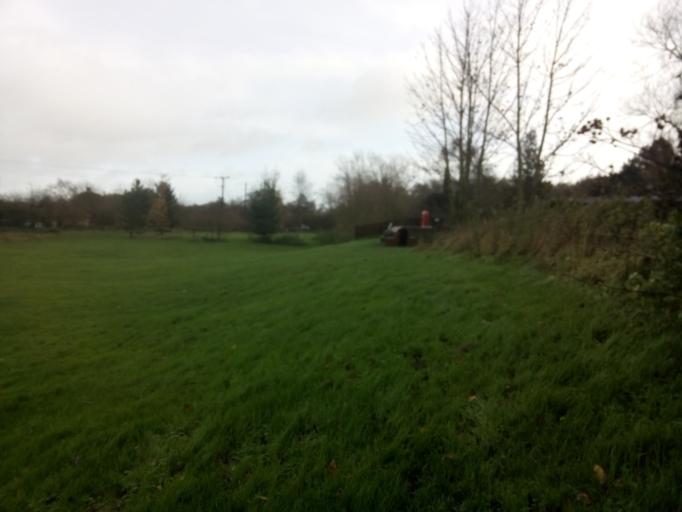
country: GB
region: England
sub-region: Suffolk
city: Needham Market
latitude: 52.1508
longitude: 1.0615
